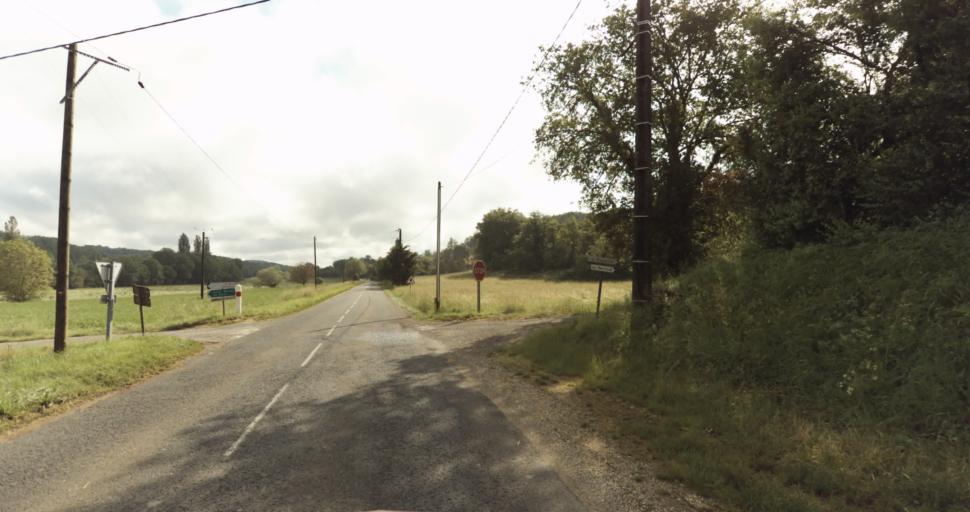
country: FR
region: Aquitaine
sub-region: Departement de la Dordogne
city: Lalinde
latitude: 44.9277
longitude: 0.7596
